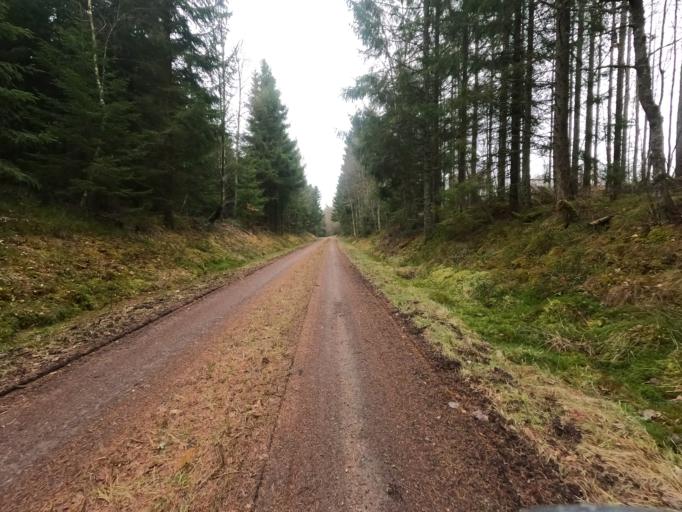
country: SE
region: Kronoberg
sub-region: Markaryds Kommun
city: Stromsnasbruk
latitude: 56.7902
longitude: 13.6286
